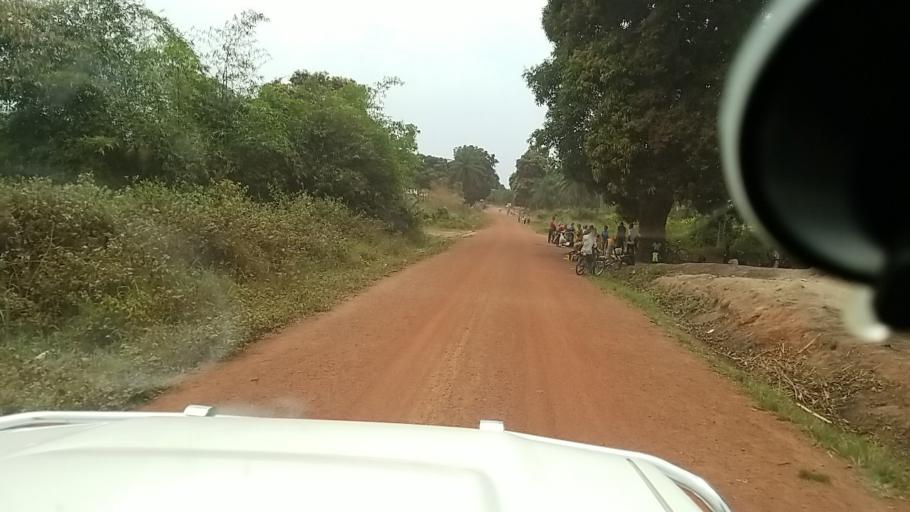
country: CD
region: Equateur
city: Libenge
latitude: 3.7301
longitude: 18.7737
